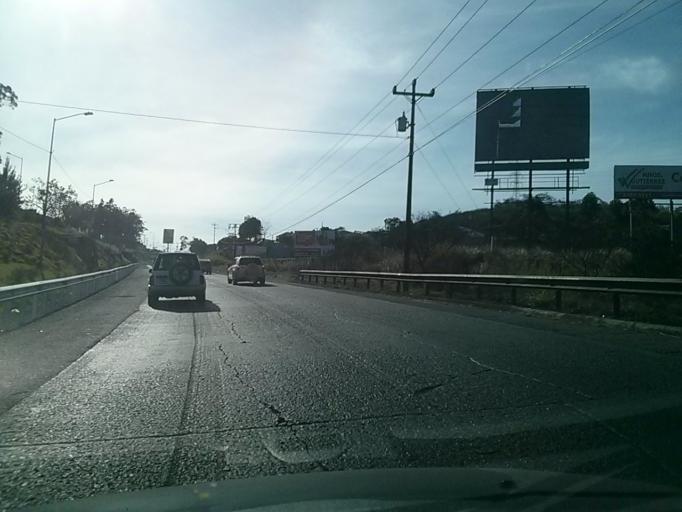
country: CR
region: Cartago
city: Cartago
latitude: 9.8901
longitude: -83.9361
